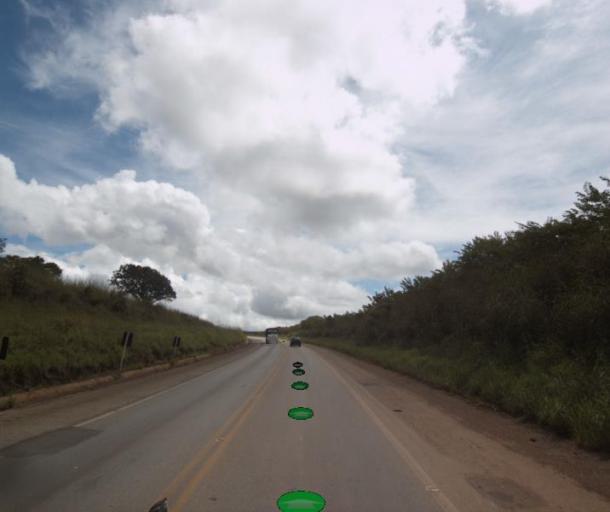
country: BR
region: Federal District
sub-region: Brasilia
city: Brasilia
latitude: -15.7459
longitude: -48.3543
